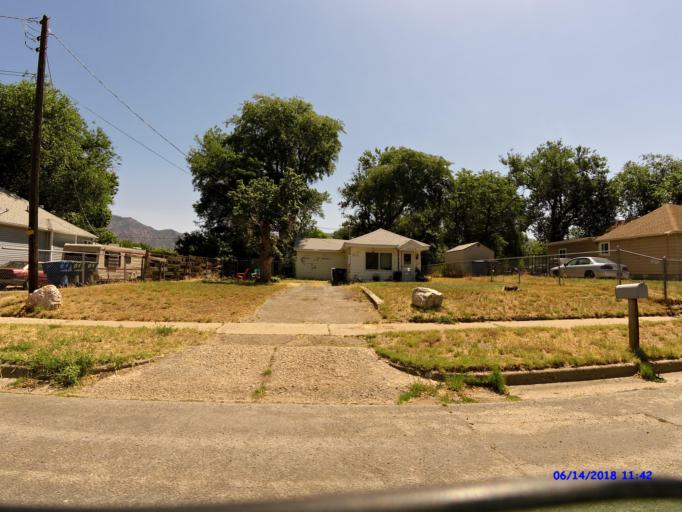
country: US
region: Utah
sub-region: Weber County
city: Ogden
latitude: 41.2214
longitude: -111.9972
